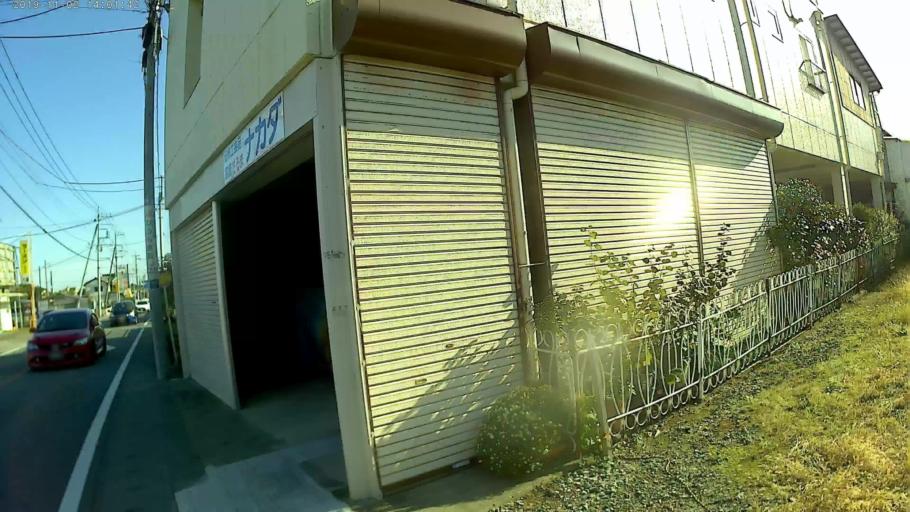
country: JP
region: Gunma
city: Takasaki
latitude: 36.3348
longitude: 138.9826
